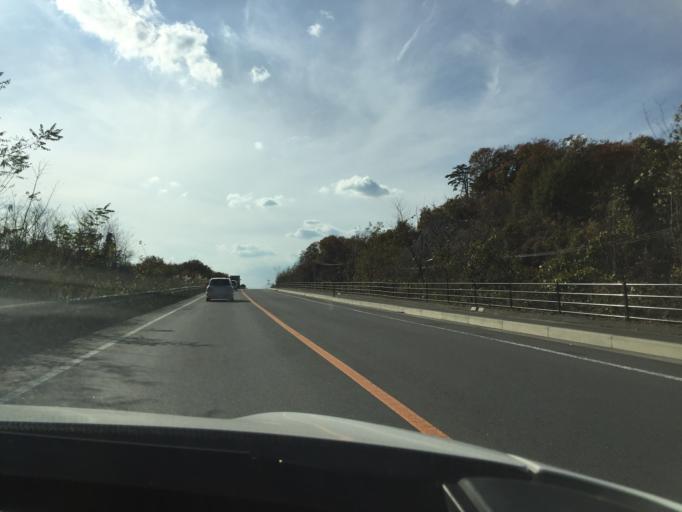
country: JP
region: Fukushima
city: Miharu
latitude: 37.4400
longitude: 140.4596
